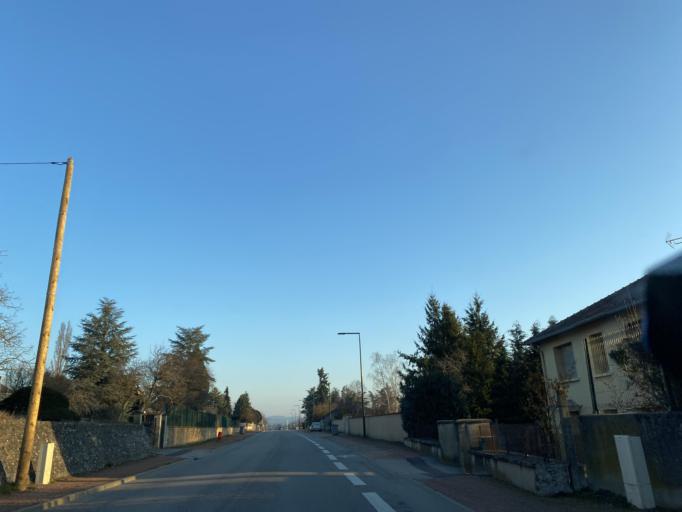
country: FR
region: Rhone-Alpes
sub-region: Departement de la Loire
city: Saint-Germain-Laval
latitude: 45.8336
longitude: 4.0149
